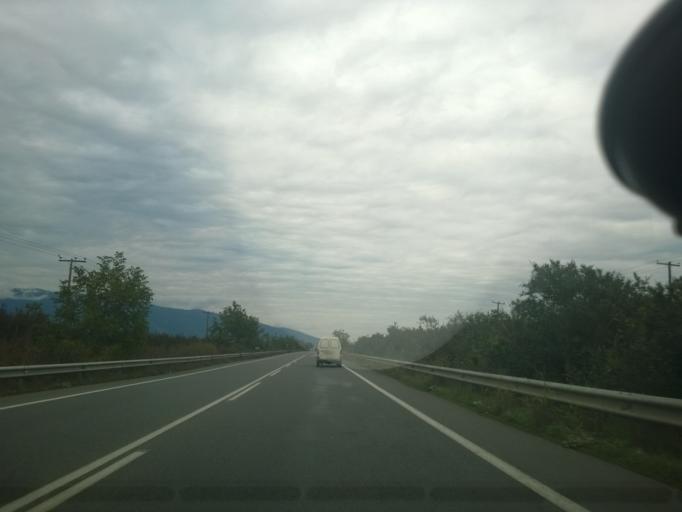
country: GR
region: Central Macedonia
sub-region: Nomos Pellis
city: Mavrovouni
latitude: 40.7900
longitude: 22.1671
